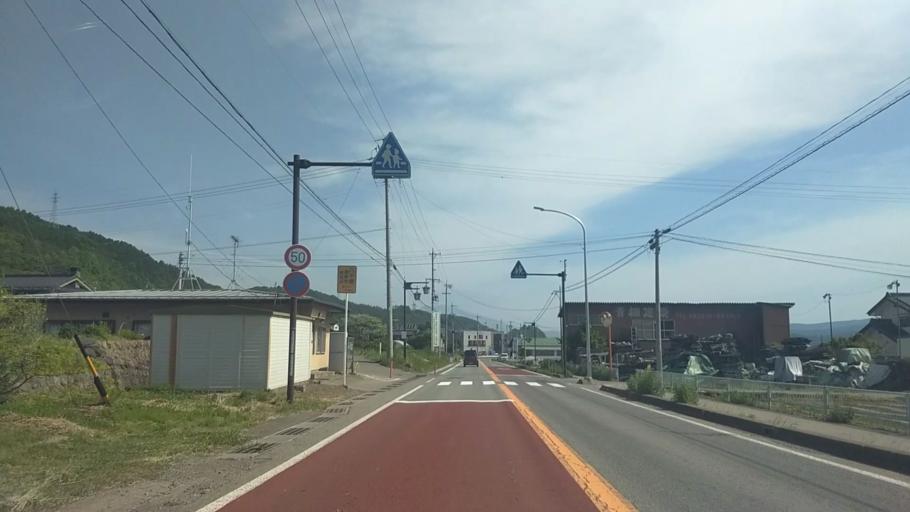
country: JP
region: Nagano
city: Saku
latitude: 36.1406
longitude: 138.4717
